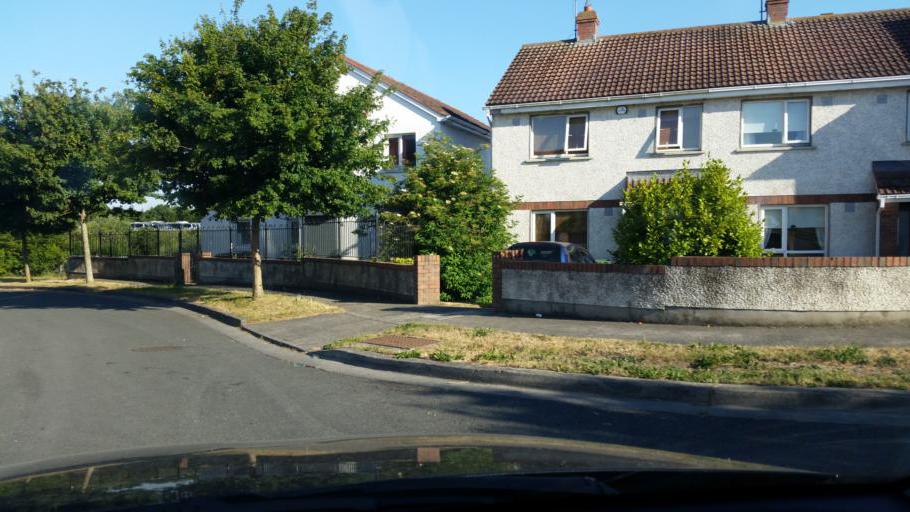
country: IE
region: Leinster
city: Ballymun
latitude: 53.4518
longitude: -6.2919
